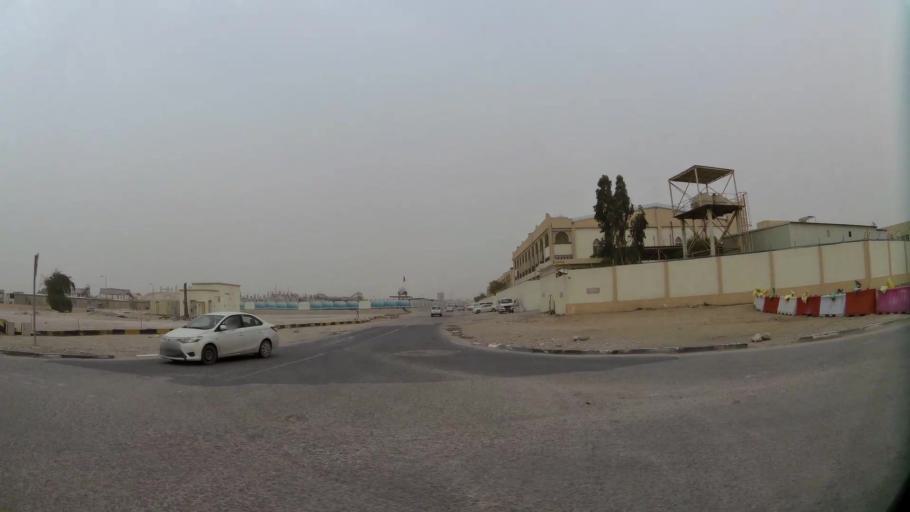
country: QA
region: Baladiyat ad Dawhah
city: Doha
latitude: 25.2371
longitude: 51.5055
